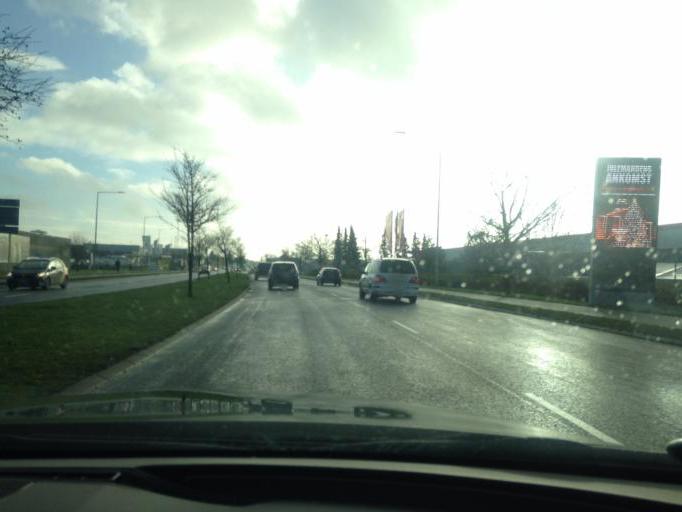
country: DK
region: South Denmark
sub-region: Kolding Kommune
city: Kolding
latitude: 55.5098
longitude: 9.4555
